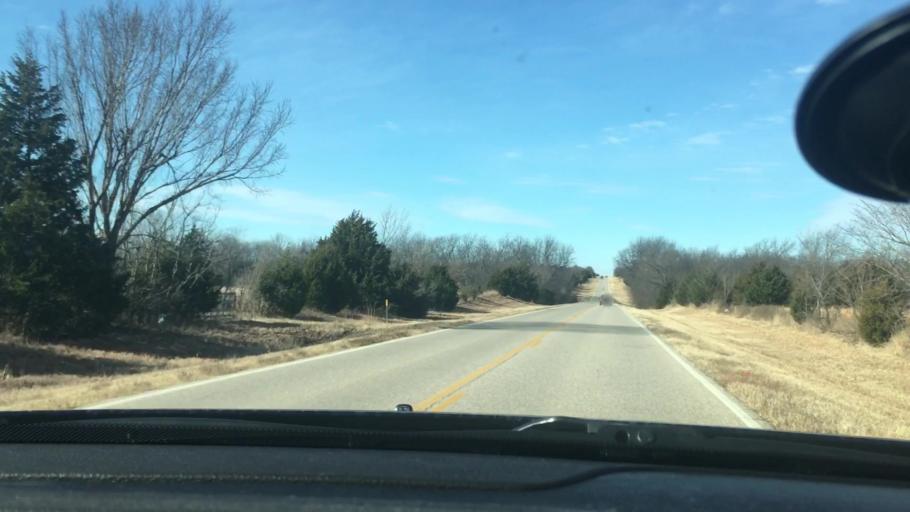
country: US
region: Oklahoma
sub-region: Garvin County
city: Stratford
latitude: 34.9859
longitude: -97.0047
